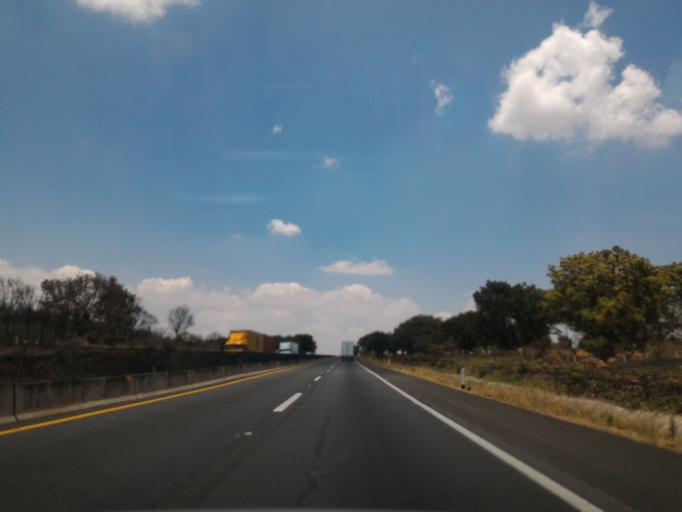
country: MX
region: Jalisco
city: Tepatitlan de Morelos
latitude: 20.8531
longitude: -102.7731
